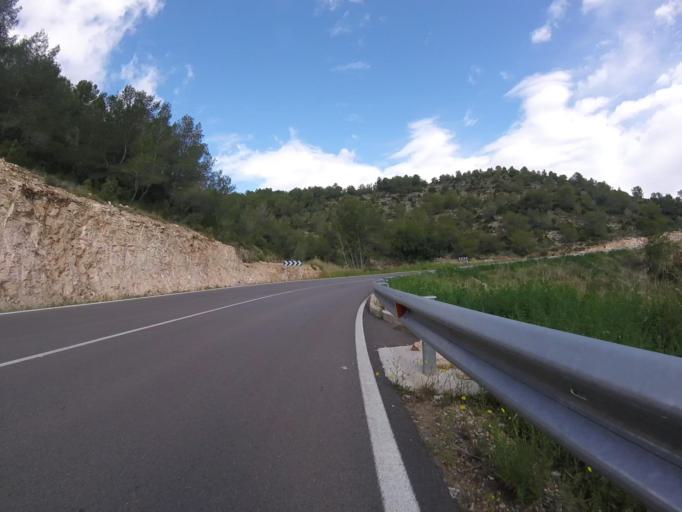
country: ES
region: Valencia
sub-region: Provincia de Castello
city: Adzaneta
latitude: 40.2711
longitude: -0.1103
